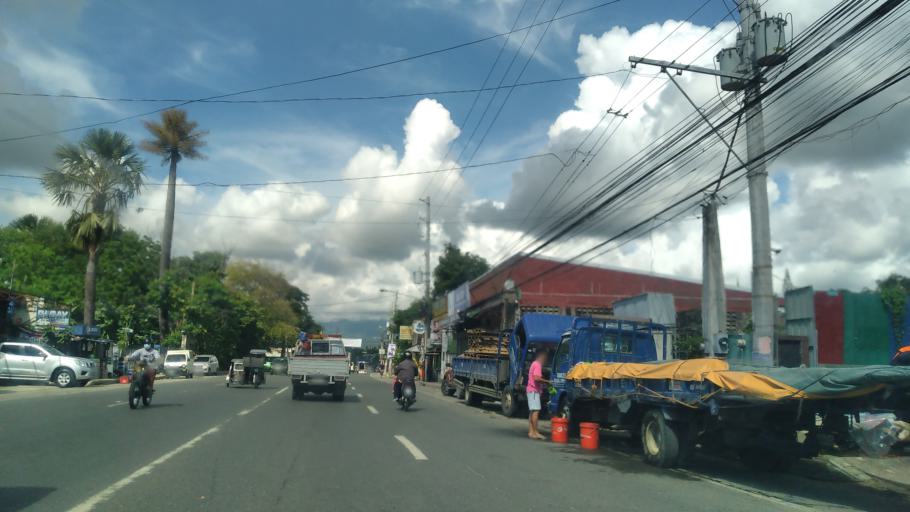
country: PH
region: Calabarzon
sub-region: Province of Quezon
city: Lucena
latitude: 13.9426
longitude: 121.5941
